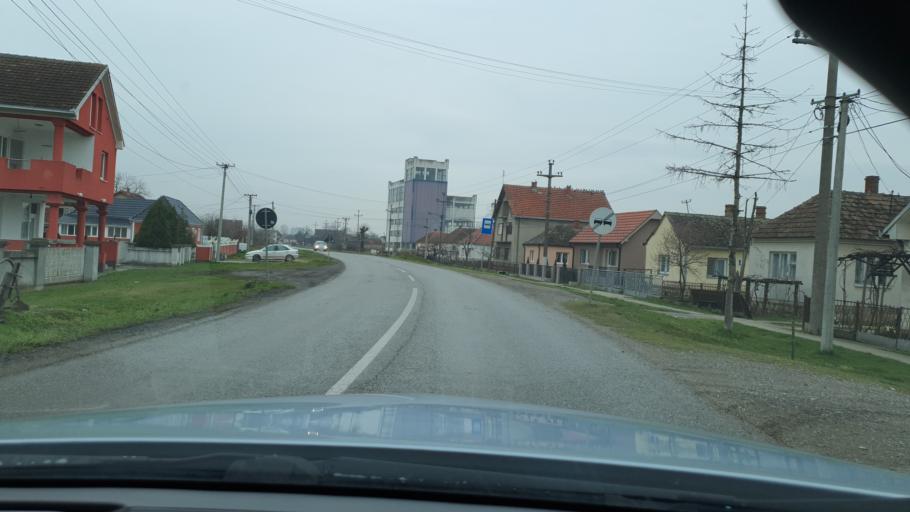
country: RS
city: Stitar
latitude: 44.7819
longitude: 19.6040
